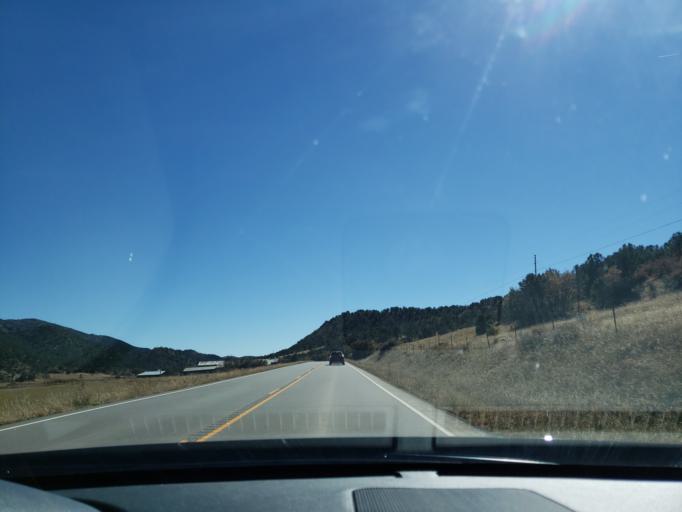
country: US
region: Colorado
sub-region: Fremont County
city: Canon City
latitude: 38.6066
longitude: -105.4372
